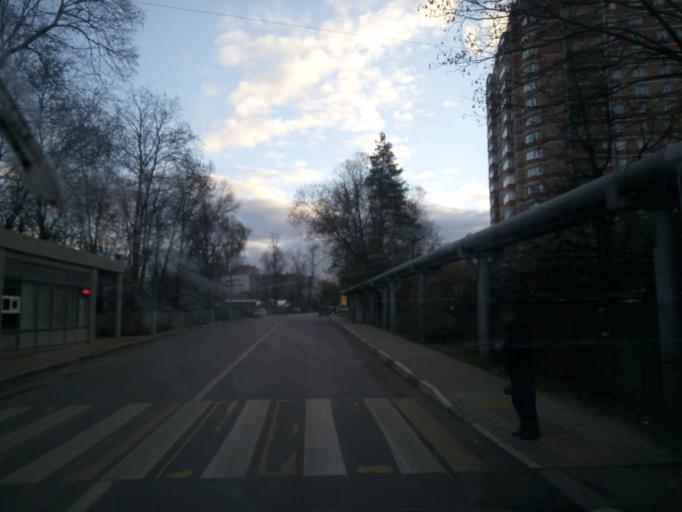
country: RU
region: Moskovskaya
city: Skhodnya
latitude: 55.9581
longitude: 37.3056
